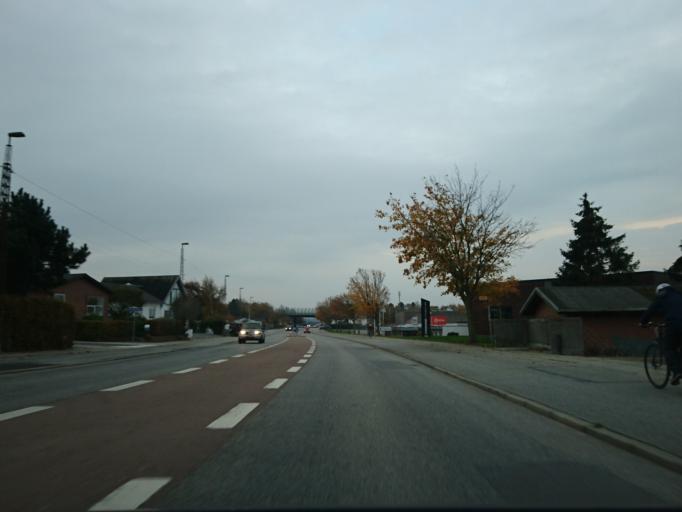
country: DK
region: North Denmark
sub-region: Alborg Kommune
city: Aalborg
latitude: 57.0148
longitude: 9.9250
